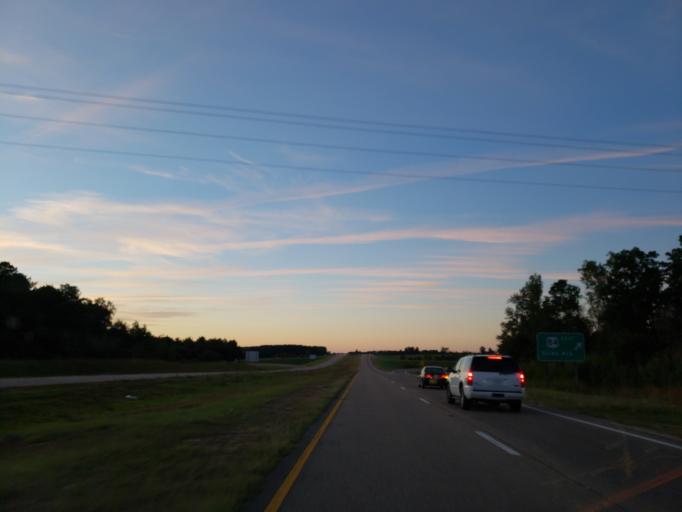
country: US
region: Mississippi
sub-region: Wayne County
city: Waynesboro
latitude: 31.7026
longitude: -88.6222
